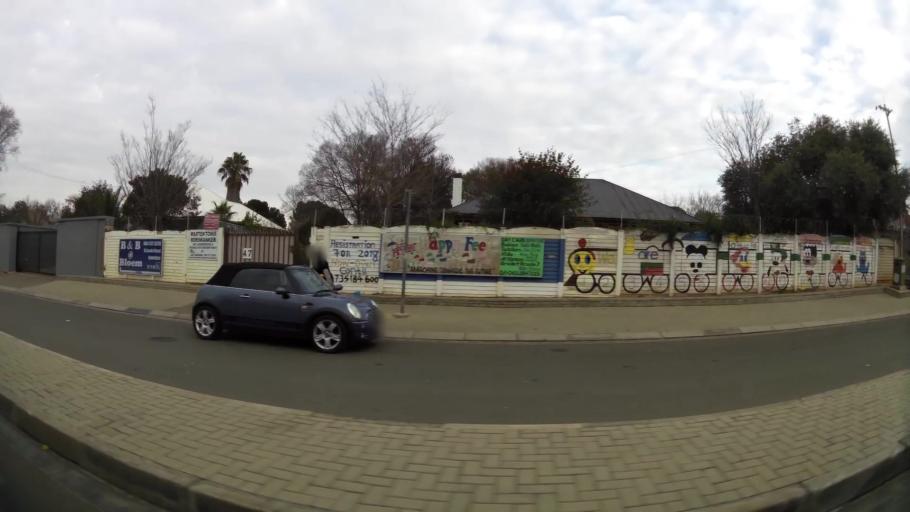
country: ZA
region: Orange Free State
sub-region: Mangaung Metropolitan Municipality
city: Bloemfontein
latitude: -29.1150
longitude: 26.2007
